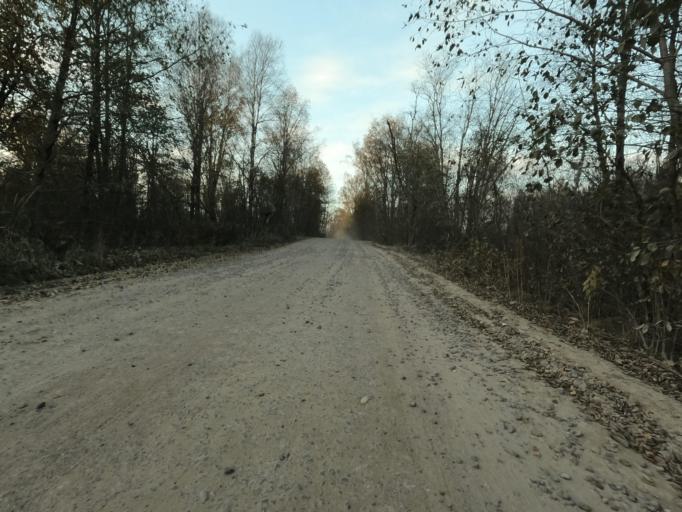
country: RU
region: Leningrad
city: Mga
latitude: 59.7733
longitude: 31.2261
